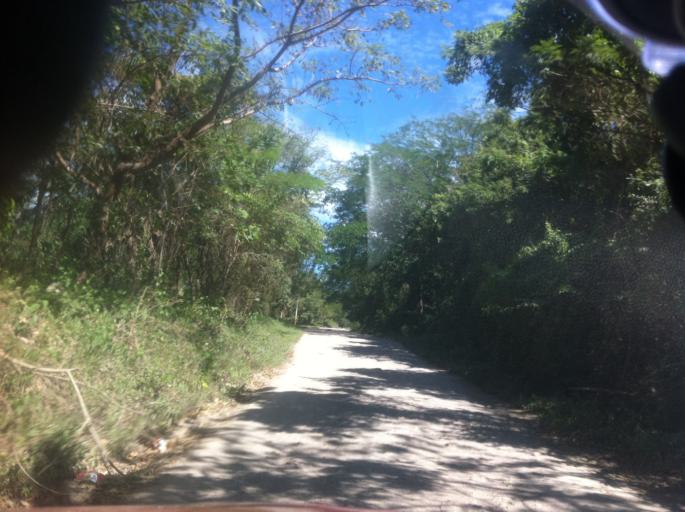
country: NI
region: Boaco
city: San Jose de los Remates
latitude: 12.6696
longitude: -85.7880
